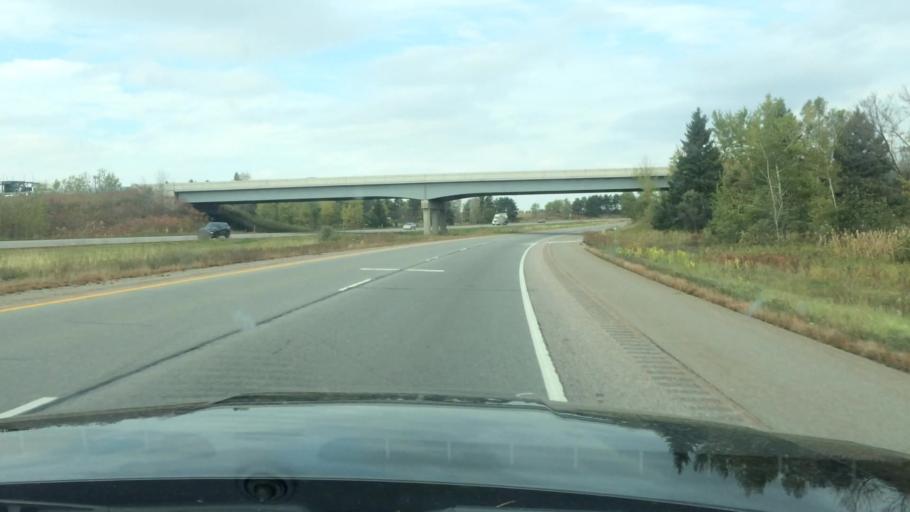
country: US
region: Wisconsin
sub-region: Marathon County
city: Mosinee
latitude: 44.7281
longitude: -89.6776
